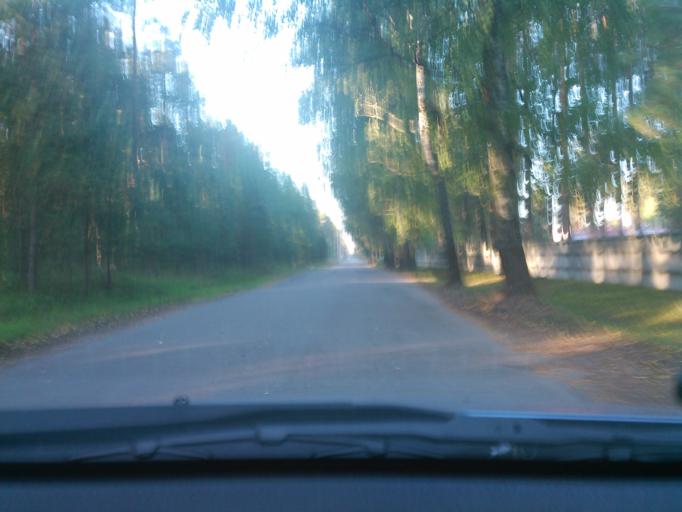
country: LV
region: Adazi
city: Adazi
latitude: 57.0966
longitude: 24.3698
